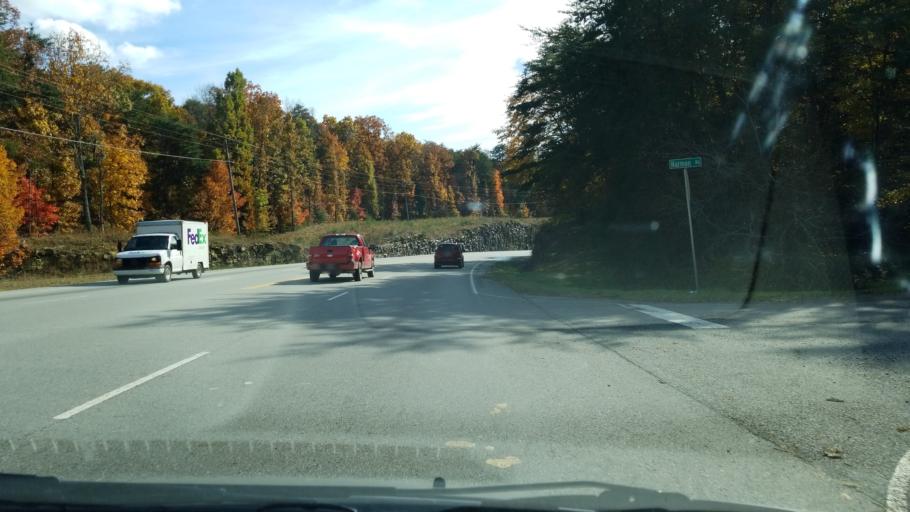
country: US
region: Tennessee
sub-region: Sequatchie County
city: Dunlap
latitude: 35.4360
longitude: -85.4205
